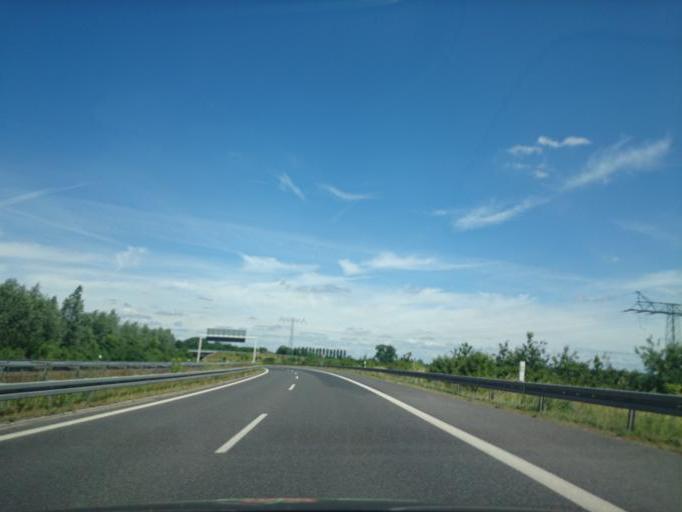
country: DE
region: Brandenburg
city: Rangsdorf
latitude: 52.3206
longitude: 13.4511
